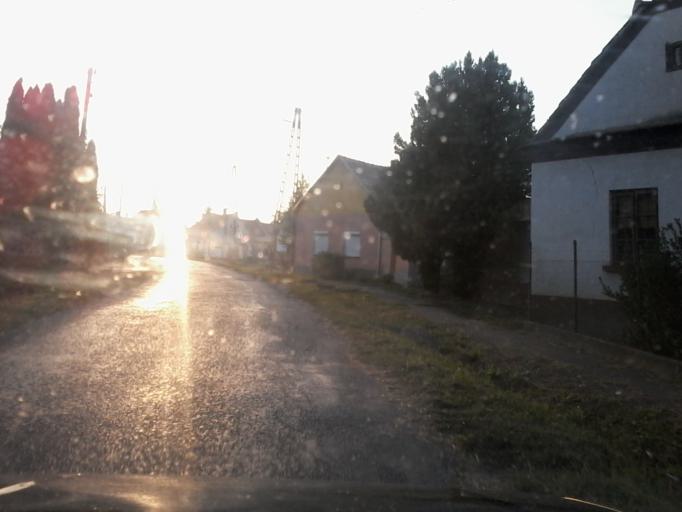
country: HU
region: Vas
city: Janoshaza
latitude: 47.0934
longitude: 17.1934
